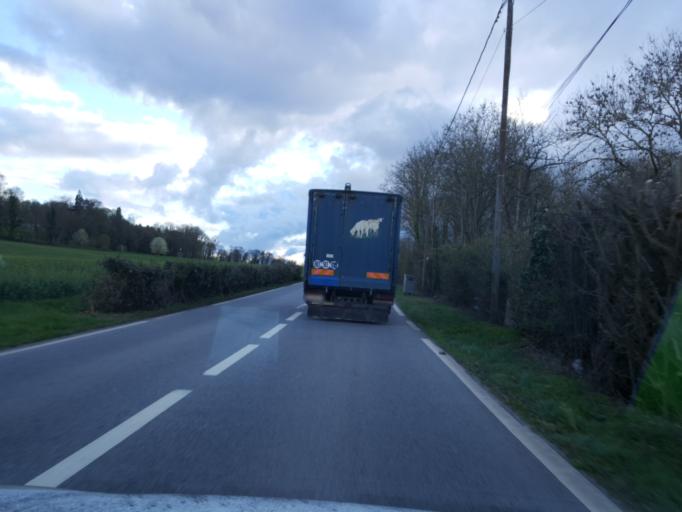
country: FR
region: Ile-de-France
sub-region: Departement des Yvelines
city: Septeuil
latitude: 48.9179
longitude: 1.6884
